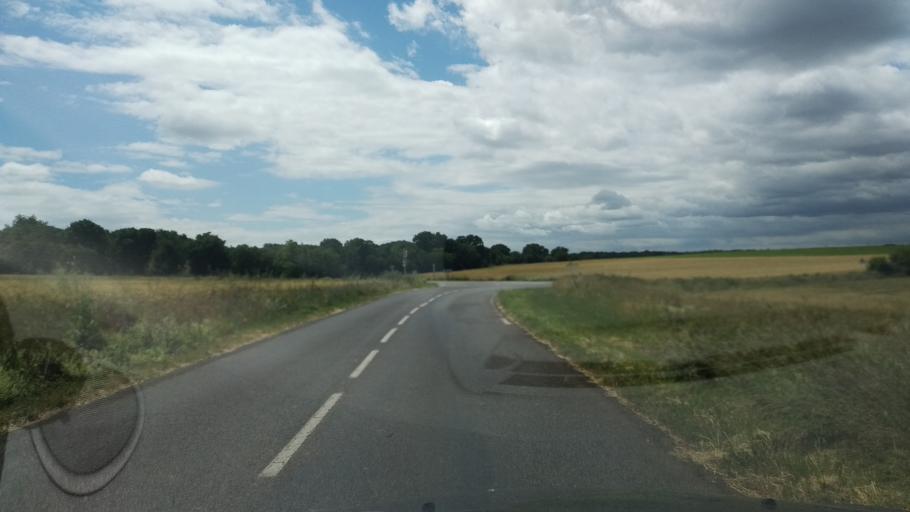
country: FR
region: Poitou-Charentes
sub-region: Departement de la Vienne
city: Vouneuil-sous-Biard
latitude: 46.6010
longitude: 0.2481
